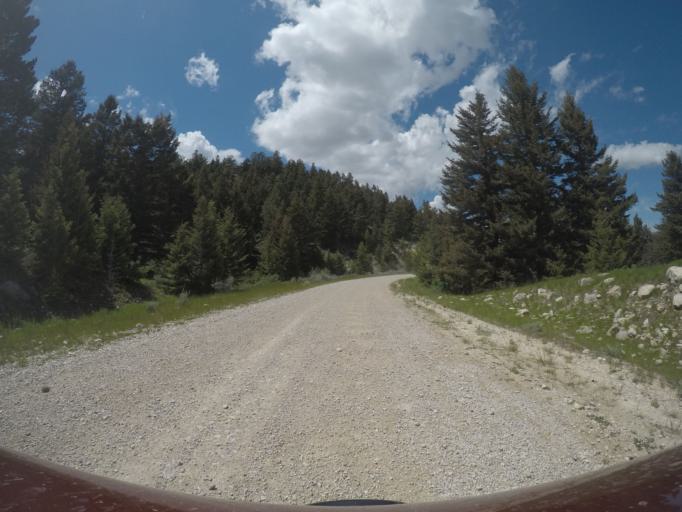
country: US
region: Wyoming
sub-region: Big Horn County
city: Lovell
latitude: 45.2065
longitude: -108.5412
